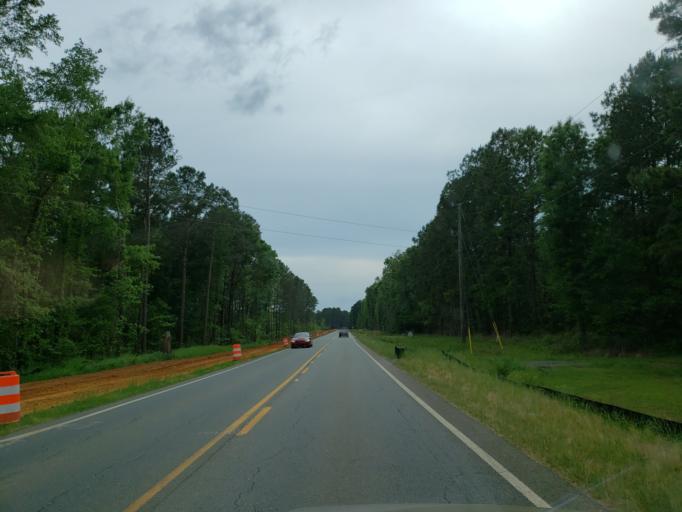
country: US
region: Georgia
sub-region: Macon County
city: Marshallville
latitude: 32.3826
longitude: -83.8772
